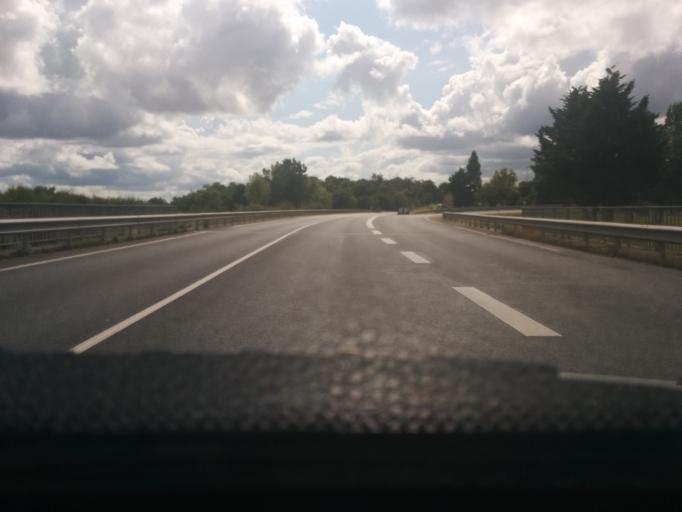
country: FR
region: Pays de la Loire
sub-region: Departement de la Vendee
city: Mortagne-sur-Sevre
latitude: 46.9875
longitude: -0.9402
